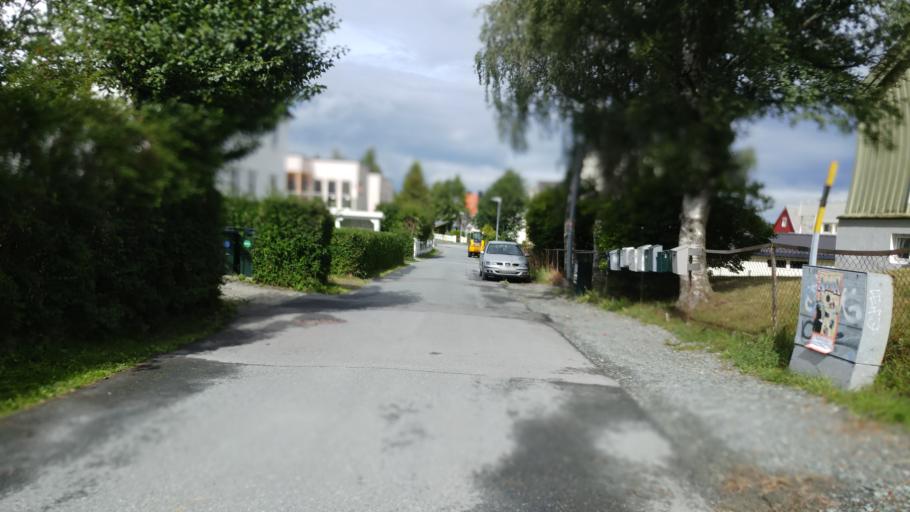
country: NO
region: Sor-Trondelag
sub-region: Trondheim
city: Trondheim
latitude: 63.4343
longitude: 10.4463
